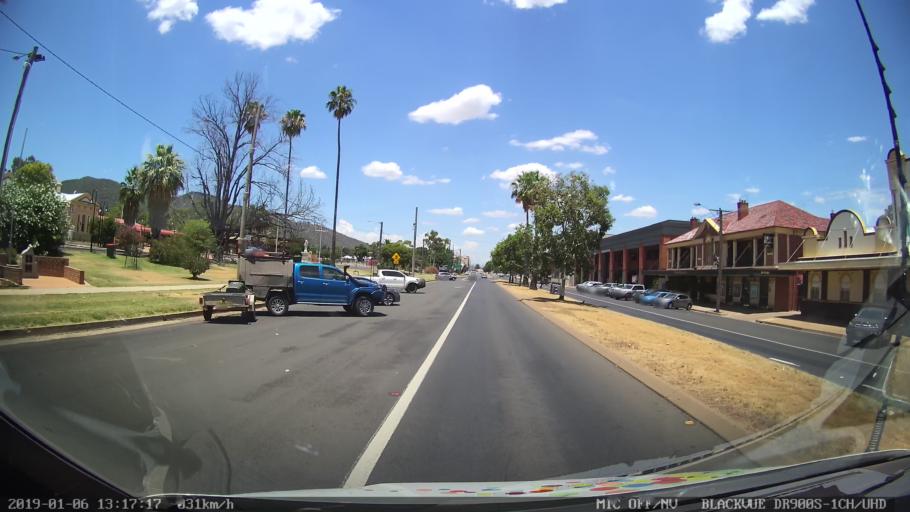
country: AU
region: New South Wales
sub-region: Tamworth Municipality
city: Tamworth
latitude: -31.0874
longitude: 150.9301
